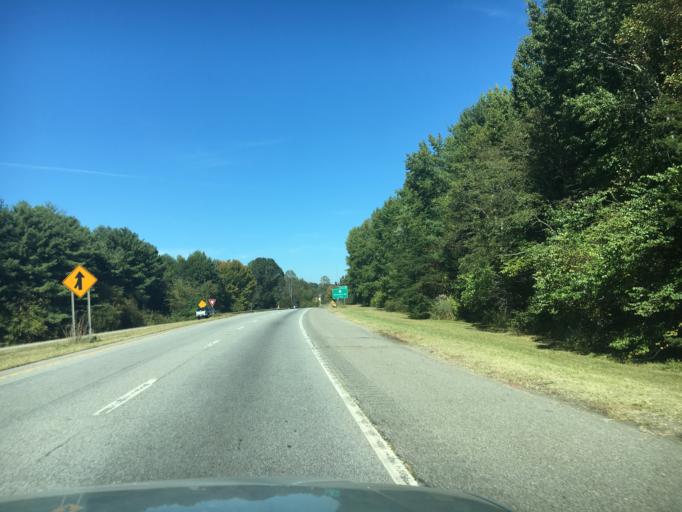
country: US
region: North Carolina
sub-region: Buncombe County
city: Bent Creek
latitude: 35.5550
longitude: -82.6092
